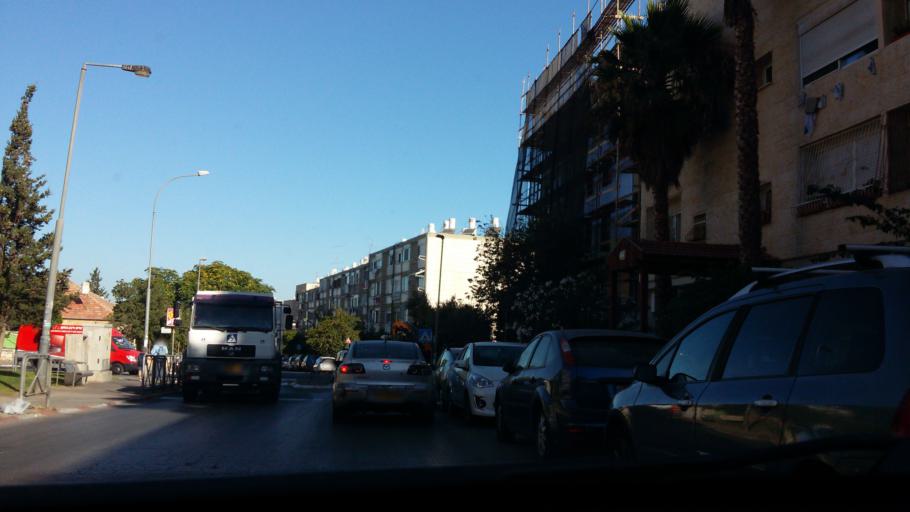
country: IL
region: Jerusalem
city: Jerusalem
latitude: 31.7546
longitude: 35.2181
